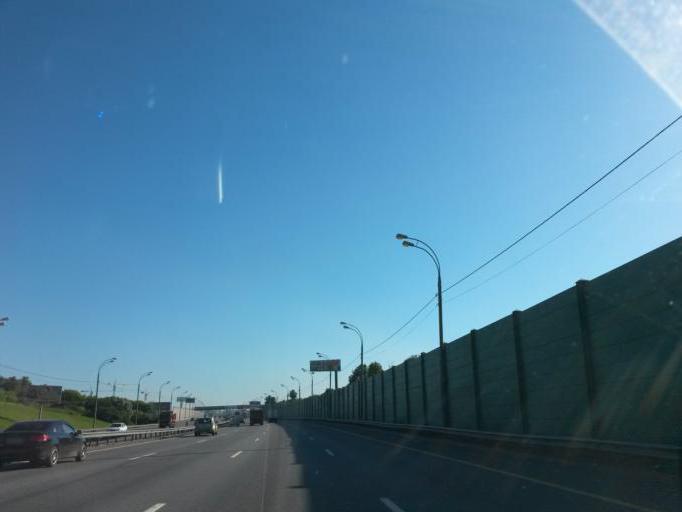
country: RU
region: Moskovskaya
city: Vidnoye
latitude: 55.5570
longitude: 37.6859
